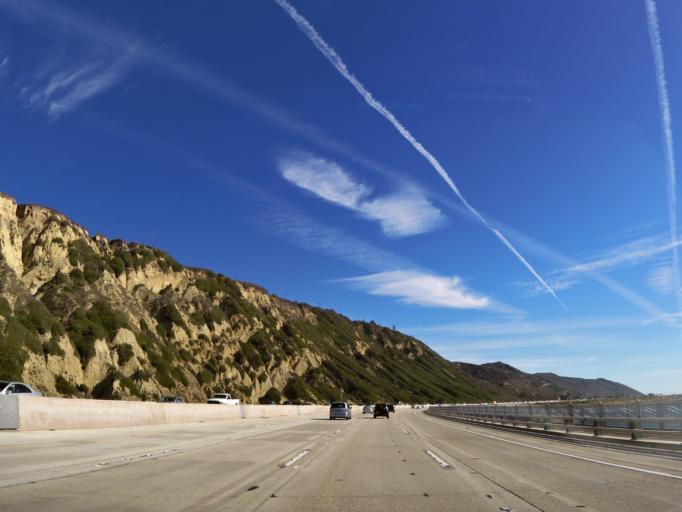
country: US
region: California
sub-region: Santa Barbara County
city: Carpinteria
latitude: 34.3560
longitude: -119.4339
